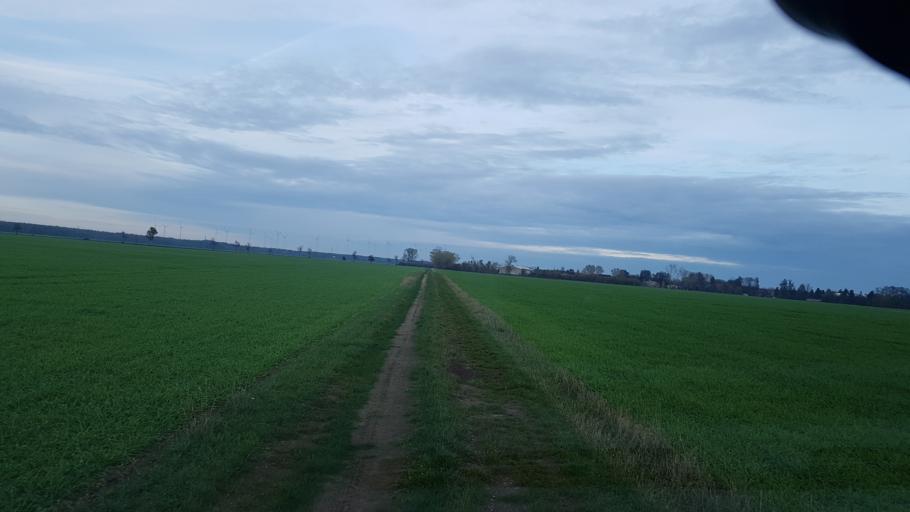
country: DE
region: Brandenburg
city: Falkenberg
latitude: 51.5375
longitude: 13.2705
